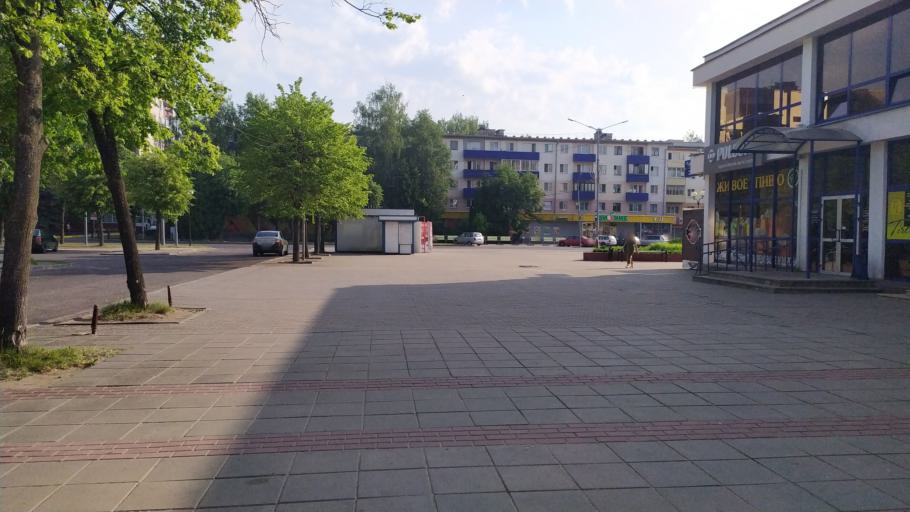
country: BY
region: Vitebsk
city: Navapolatsk
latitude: 55.5333
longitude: 28.6525
